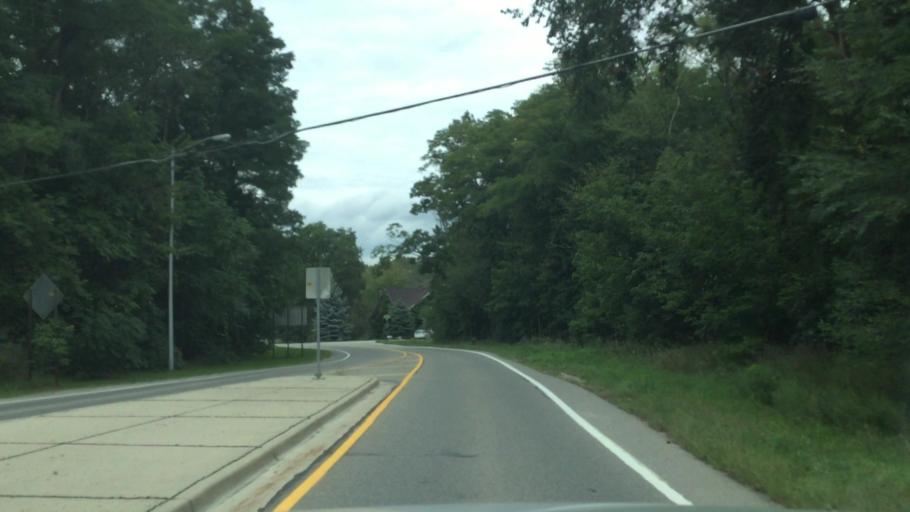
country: US
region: Michigan
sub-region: Livingston County
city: Whitmore Lake
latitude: 42.4640
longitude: -83.7985
